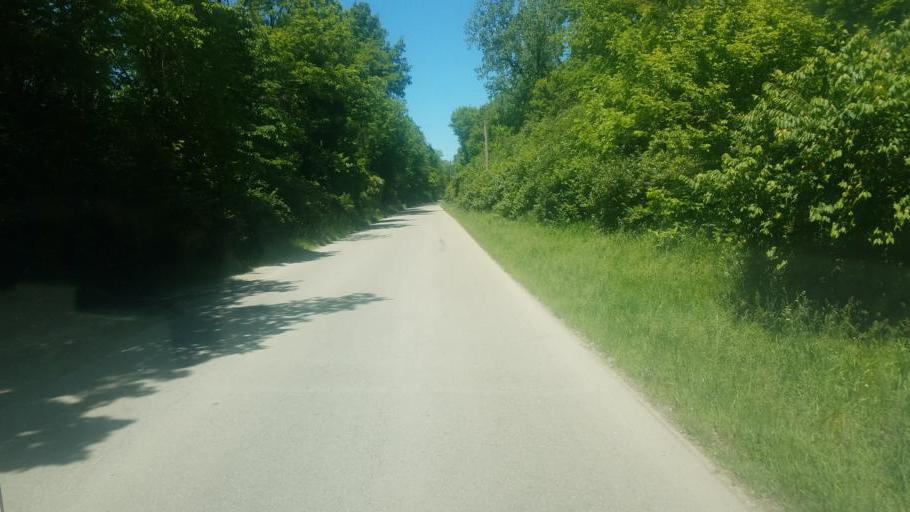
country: US
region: Ohio
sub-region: Miami County
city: Piqua
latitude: 40.2131
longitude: -84.2135
